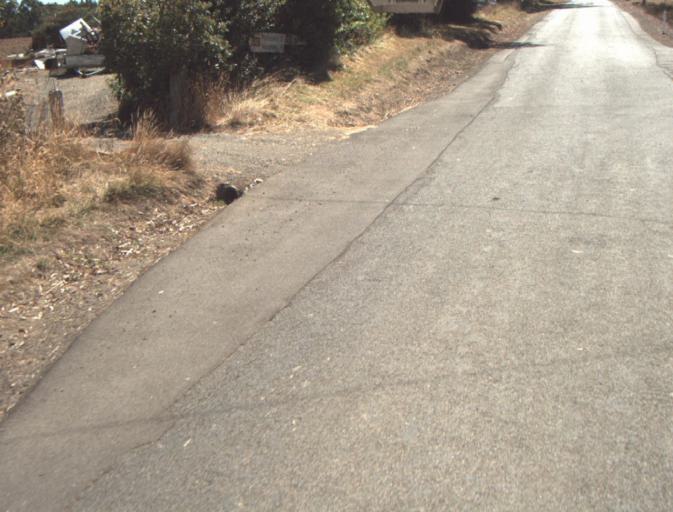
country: AU
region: Tasmania
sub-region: Launceston
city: Newstead
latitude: -41.3216
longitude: 147.3221
